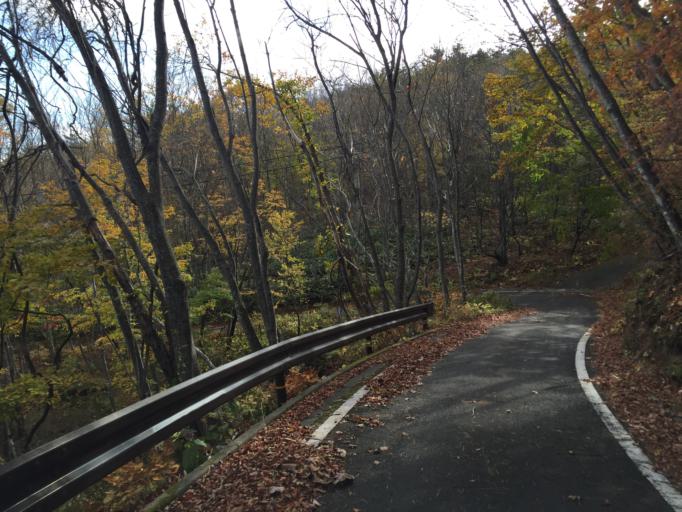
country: JP
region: Fukushima
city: Fukushima-shi
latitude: 37.7278
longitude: 140.3011
